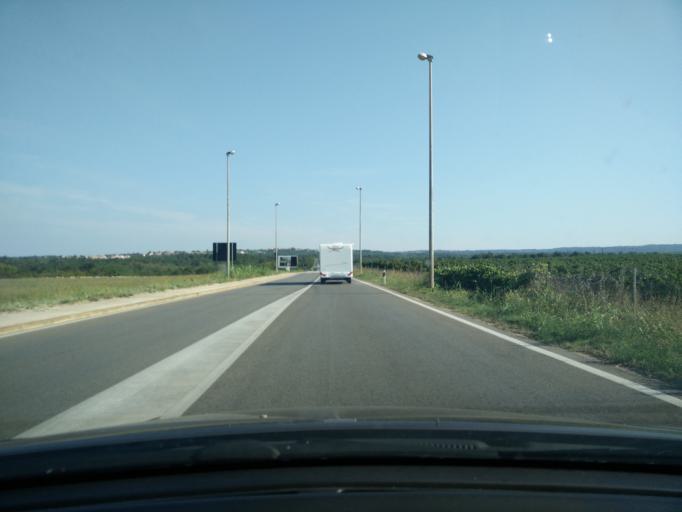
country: HR
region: Istarska
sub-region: Grad Porec
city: Porec
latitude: 45.2702
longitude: 13.6145
